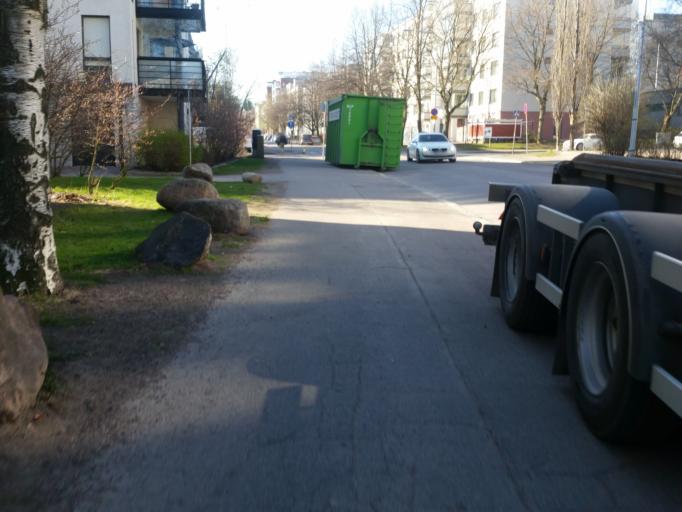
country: FI
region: Uusimaa
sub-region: Helsinki
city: Helsinki
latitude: 60.1542
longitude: 24.8848
